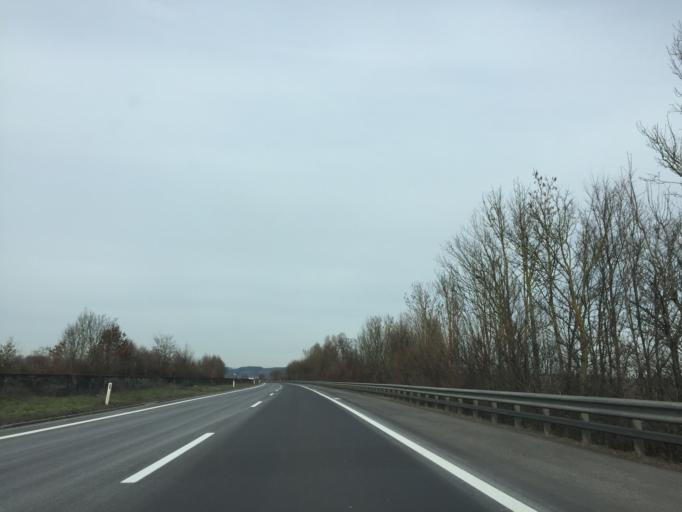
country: AT
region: Upper Austria
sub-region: Politischer Bezirk Ried im Innkreis
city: Ried im Innkreis
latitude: 48.2938
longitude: 13.4830
